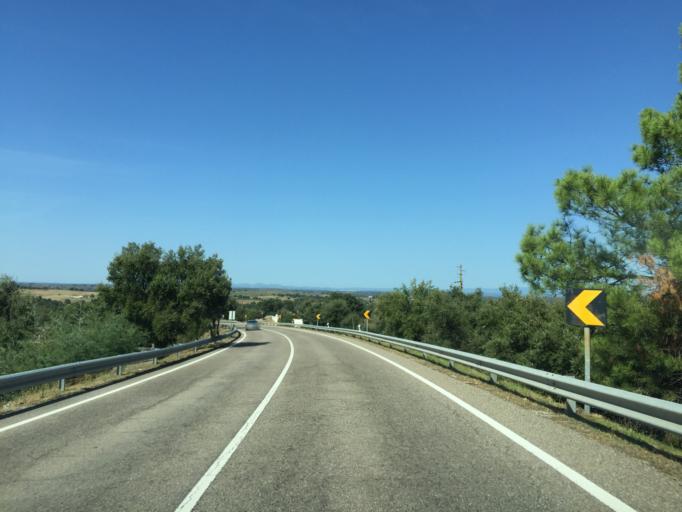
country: PT
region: Portalegre
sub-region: Castelo de Vide
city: Castelo de Vide
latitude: 39.4279
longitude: -7.4850
